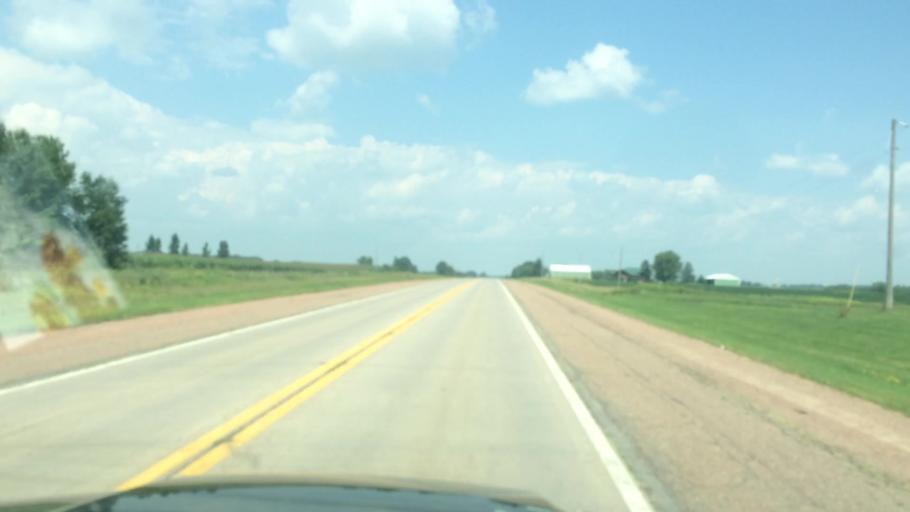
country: US
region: Wisconsin
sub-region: Clark County
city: Colby
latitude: 44.8619
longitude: -90.3158
